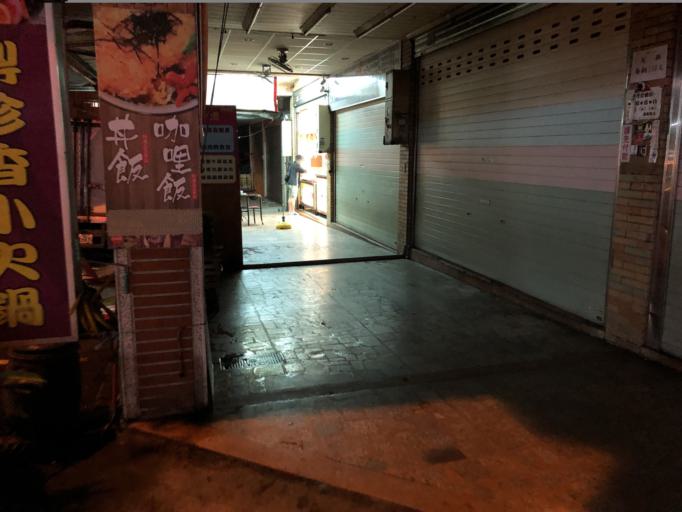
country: TW
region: Taiwan
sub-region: Taoyuan
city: Taoyuan
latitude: 24.9893
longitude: 121.3441
